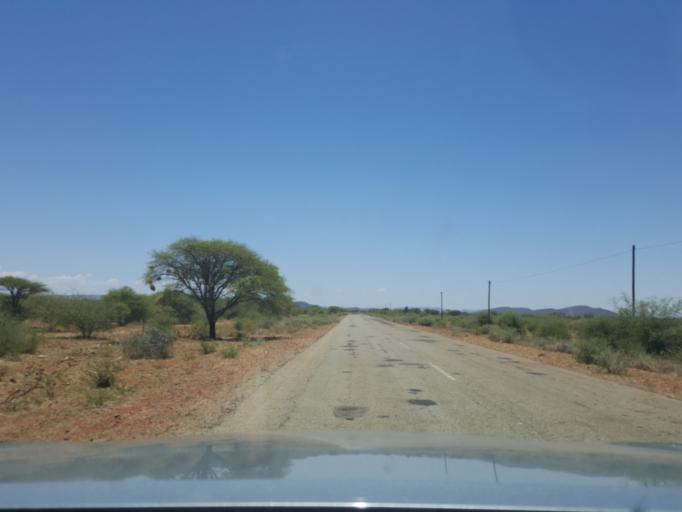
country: BW
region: South East
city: Ramotswa
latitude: -25.0133
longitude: 25.9062
